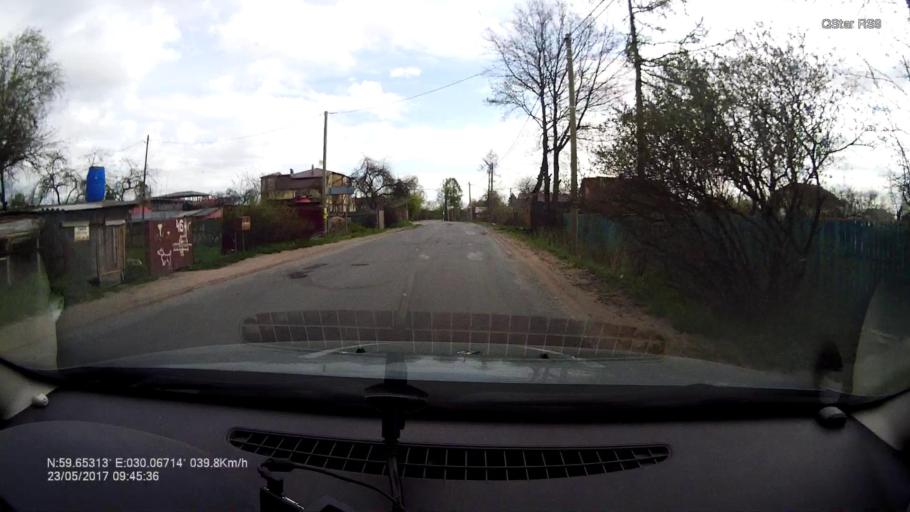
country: RU
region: Leningrad
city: Taytsy
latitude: 59.6531
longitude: 30.0675
